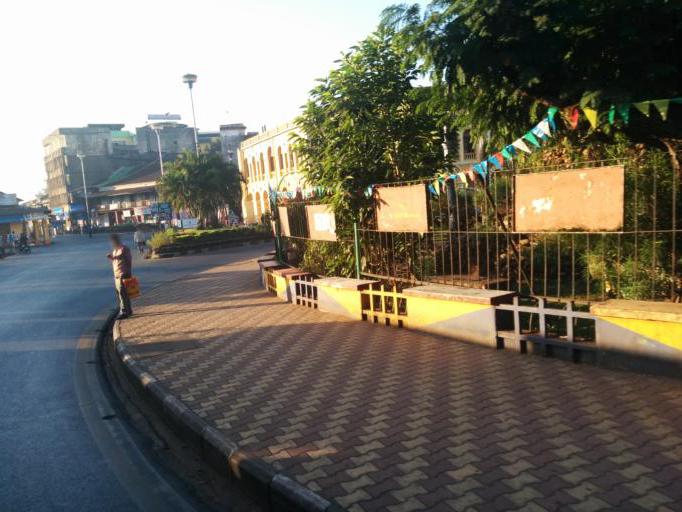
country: IN
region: Goa
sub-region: South Goa
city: Madgaon
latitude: 15.2727
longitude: 73.9586
